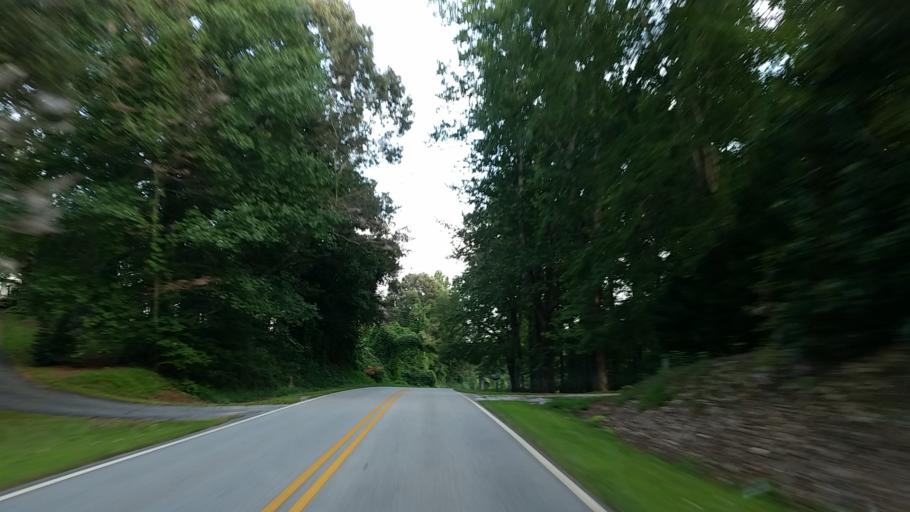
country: US
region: Georgia
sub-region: Lumpkin County
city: Dahlonega
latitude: 34.5846
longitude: -84.0252
